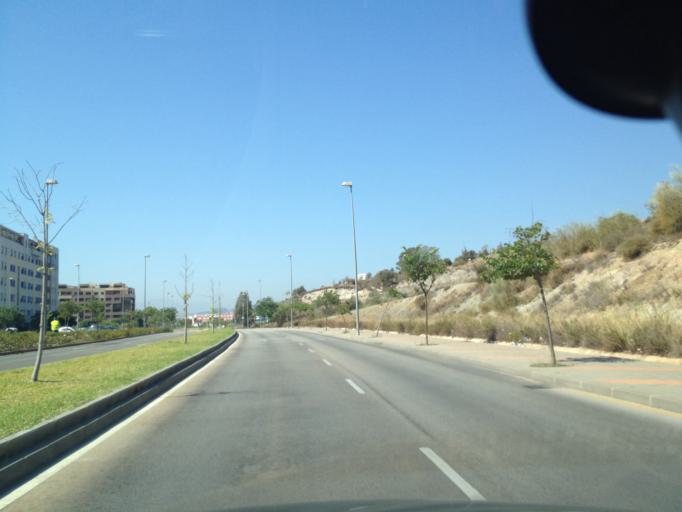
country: ES
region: Andalusia
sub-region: Provincia de Malaga
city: Malaga
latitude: 36.7264
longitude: -4.4828
